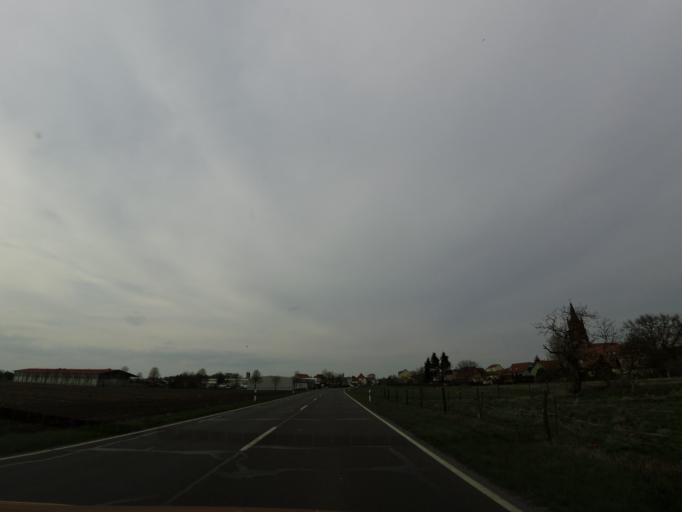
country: DE
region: Brandenburg
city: Mittenwalde
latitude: 52.2614
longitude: 13.5315
